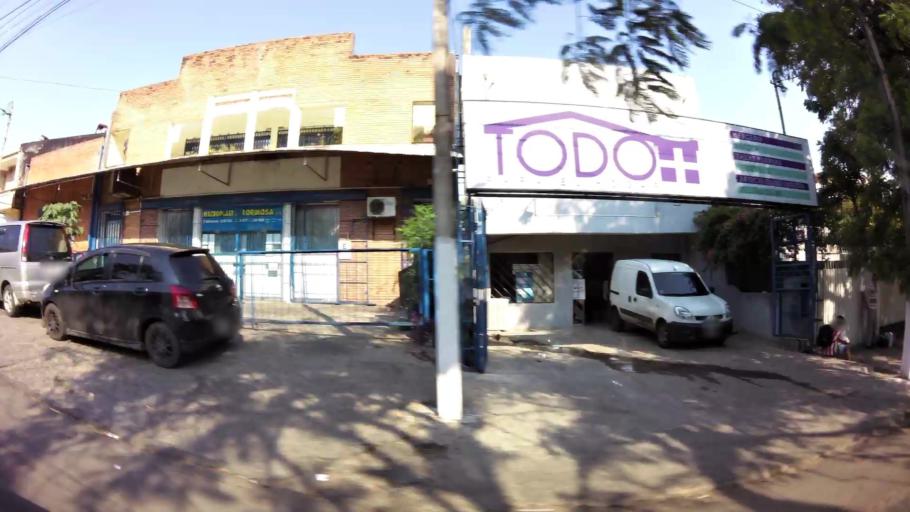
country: PY
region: Asuncion
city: Asuncion
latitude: -25.2999
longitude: -57.6269
